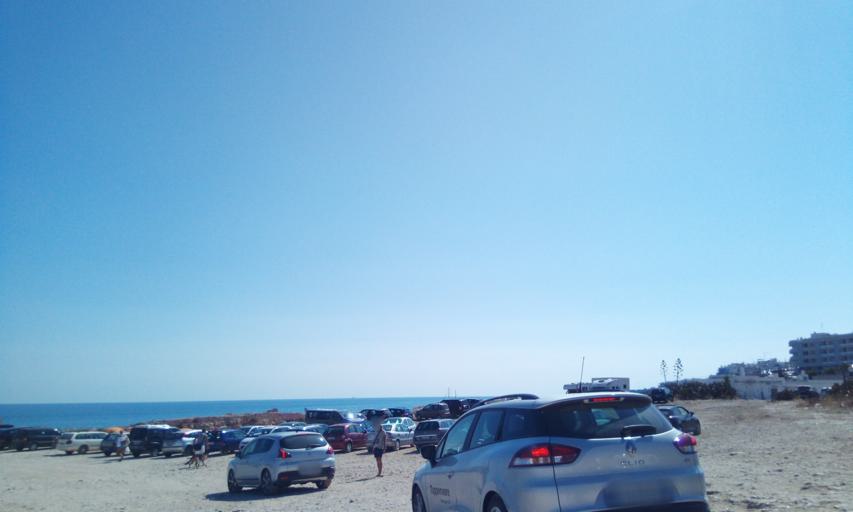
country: IT
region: Apulia
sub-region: Provincia di Bari
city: Polignano a Mare
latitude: 40.9994
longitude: 17.2126
